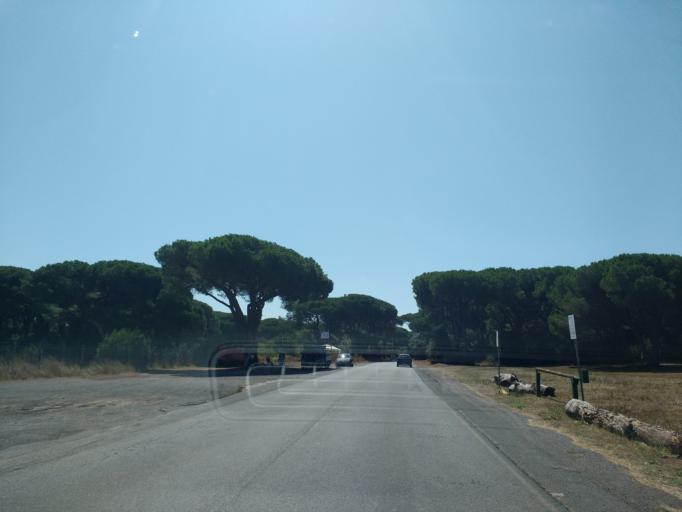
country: IT
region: Latium
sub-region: Citta metropolitana di Roma Capitale
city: Acilia-Castel Fusano-Ostia Antica
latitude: 41.7139
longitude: 12.3558
